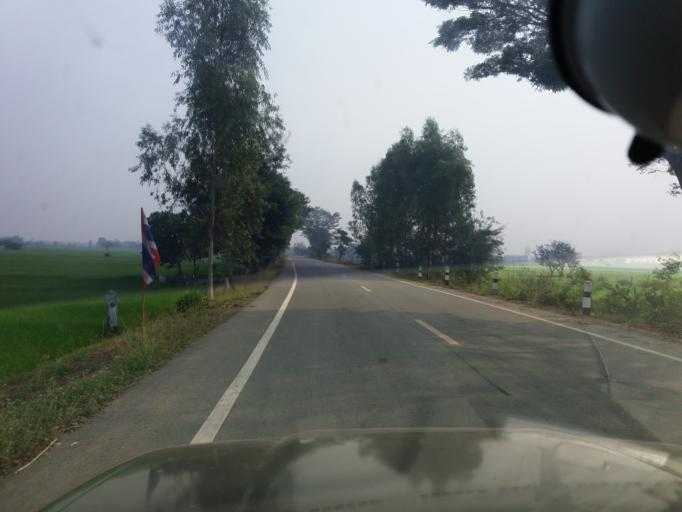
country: TH
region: Suphan Buri
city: Doem Bang Nang Buat
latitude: 14.8554
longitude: 100.1509
